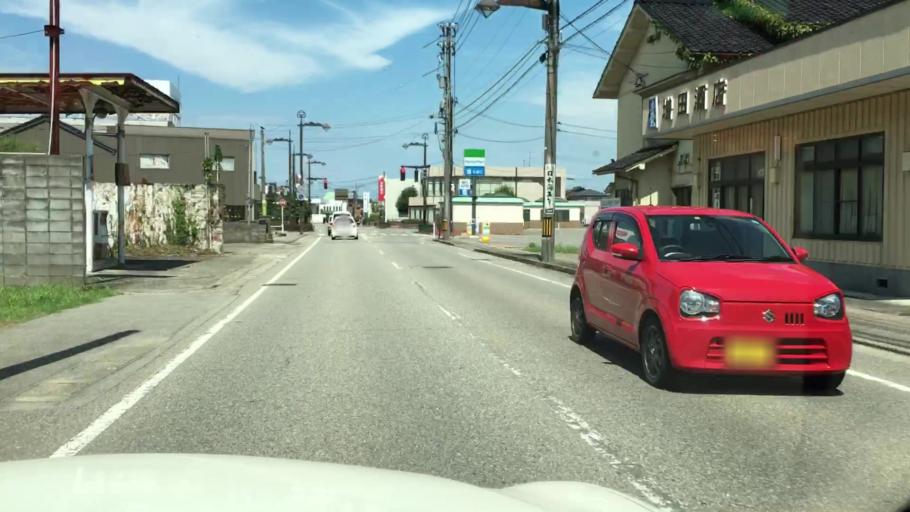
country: JP
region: Toyama
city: Kamiichi
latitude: 36.7034
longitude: 137.3581
